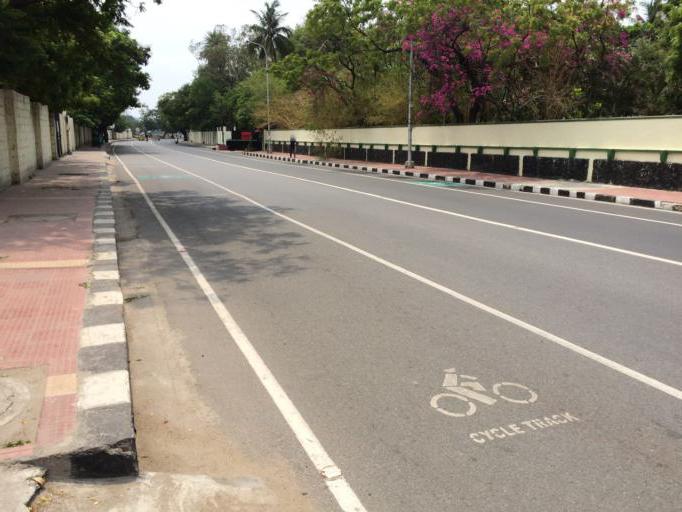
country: IN
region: Tamil Nadu
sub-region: Chennai
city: Chennai
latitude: 13.0754
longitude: 80.2845
